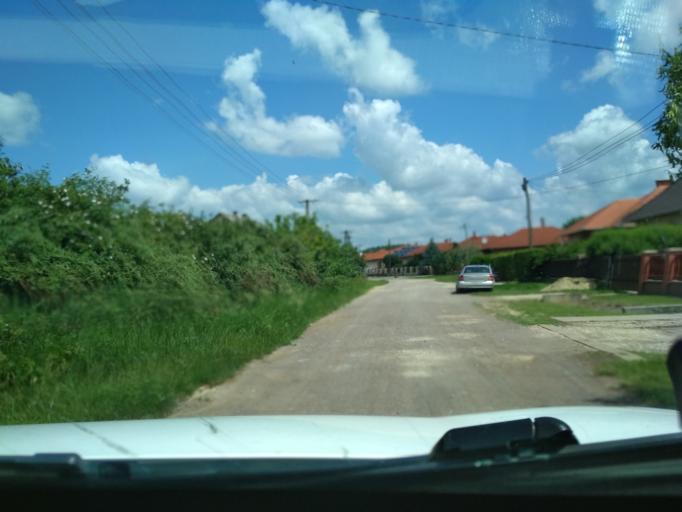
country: HU
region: Jasz-Nagykun-Szolnok
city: Tiszafured
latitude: 47.5999
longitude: 20.7570
